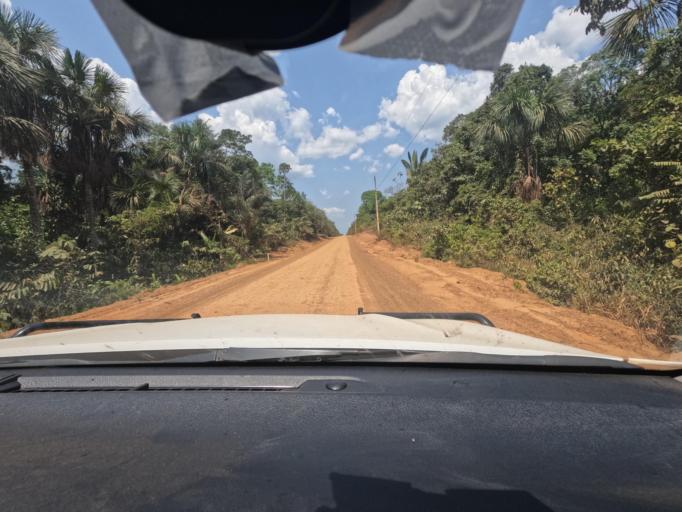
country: BR
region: Amazonas
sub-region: Humaita
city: Humaita
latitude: -7.5006
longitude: -63.6304
